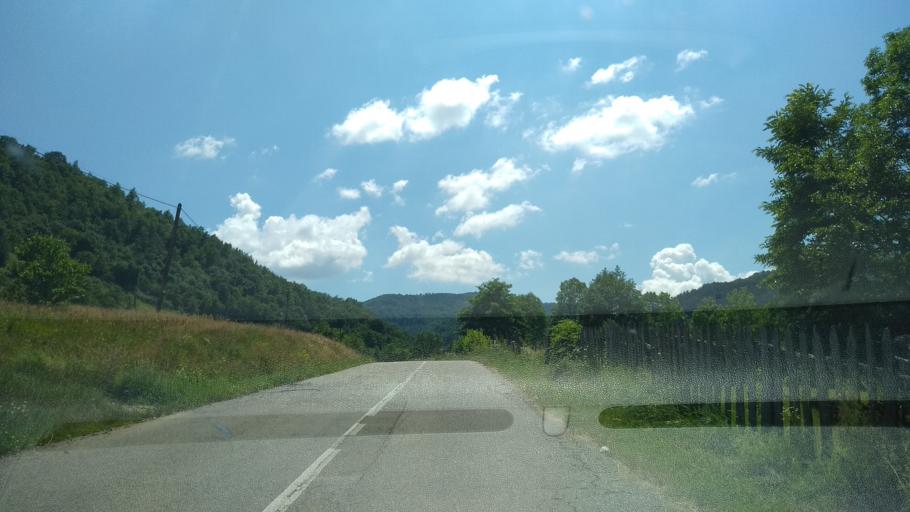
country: RO
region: Hunedoara
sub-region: Comuna Orastioara de Sus
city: Orastioara de Sus
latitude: 45.6896
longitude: 23.1621
